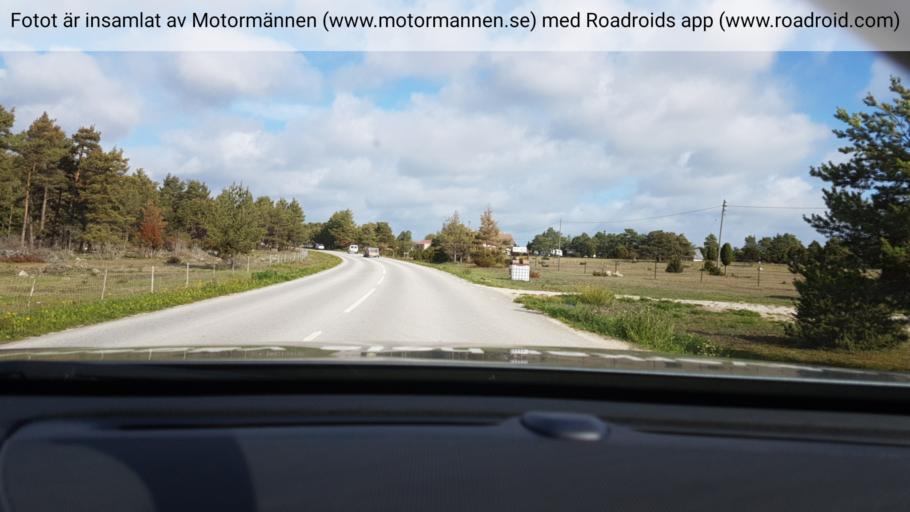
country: SE
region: Gotland
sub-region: Gotland
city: Slite
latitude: 57.8928
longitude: 19.0924
